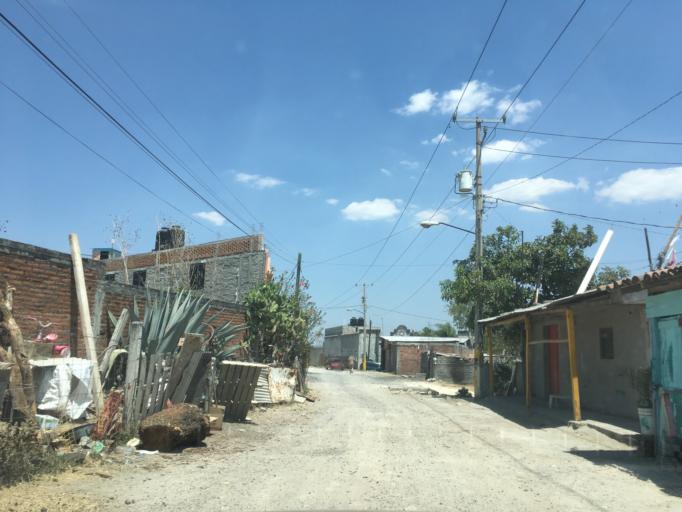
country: MX
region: Michoacan
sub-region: Morelia
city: San Antonio
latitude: 19.6699
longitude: -101.2562
